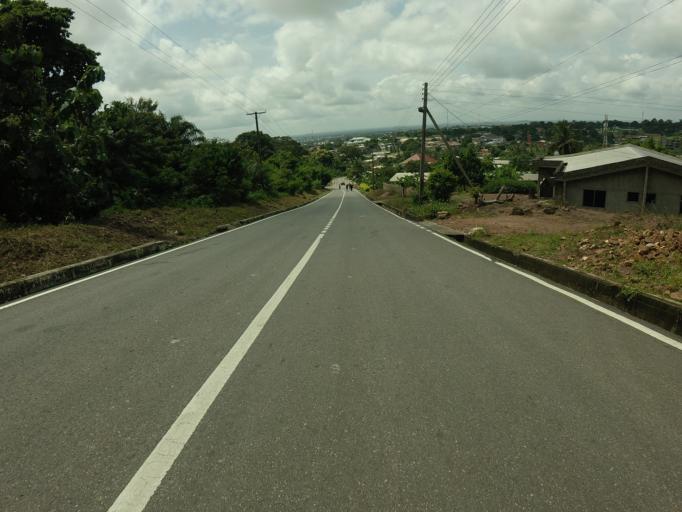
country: GH
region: Volta
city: Ho
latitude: 6.6138
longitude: 0.4553
